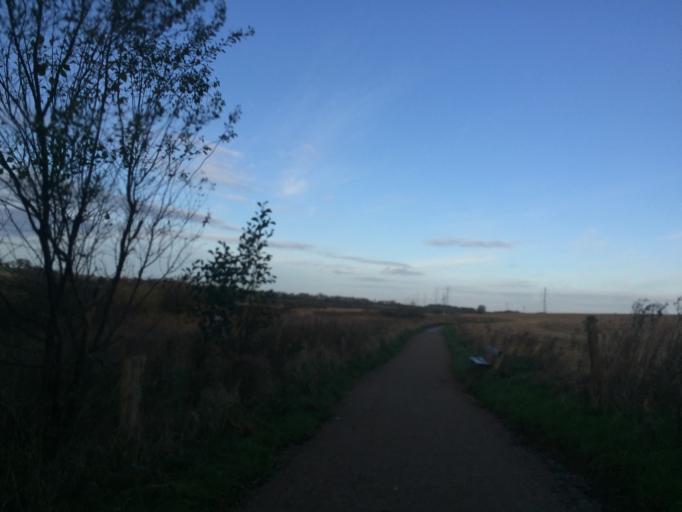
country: DK
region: Zealand
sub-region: Ringsted Kommune
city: Ringsted
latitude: 55.4509
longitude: 11.7702
